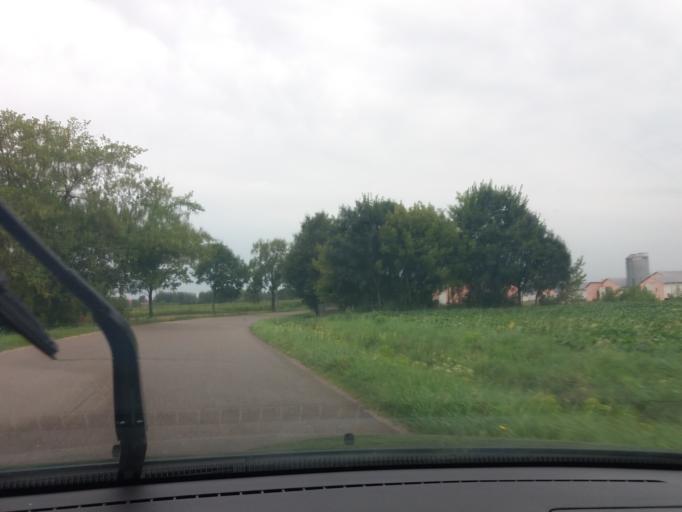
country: PL
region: Masovian Voivodeship
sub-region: Powiat mlawski
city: Wieczfnia Koscielna
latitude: 53.1889
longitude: 20.4495
